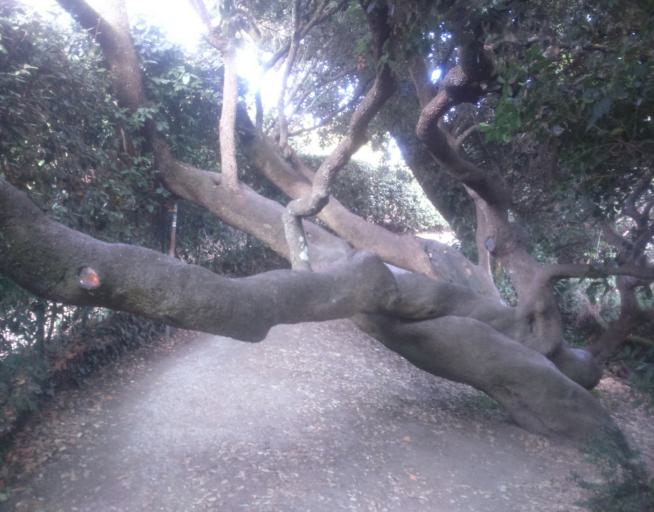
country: FR
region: Poitou-Charentes
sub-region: Departement de la Charente-Maritime
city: Saint-Palais-sur-Mer
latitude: 45.6403
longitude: -1.0938
